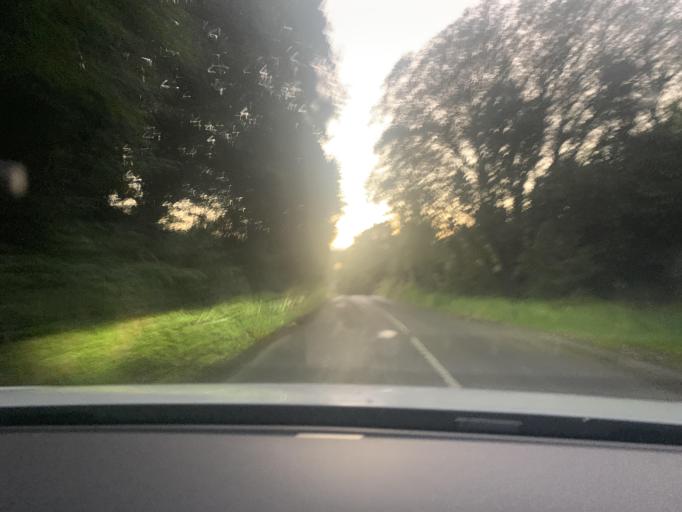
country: IE
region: Connaught
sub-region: Sligo
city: Sligo
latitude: 54.2745
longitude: -8.3325
